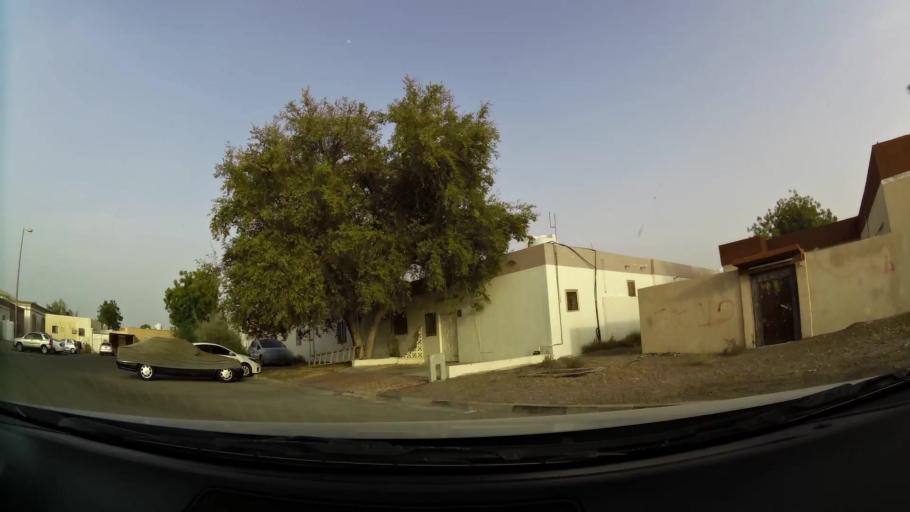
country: OM
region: Al Buraimi
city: Al Buraymi
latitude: 24.2449
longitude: 55.7441
